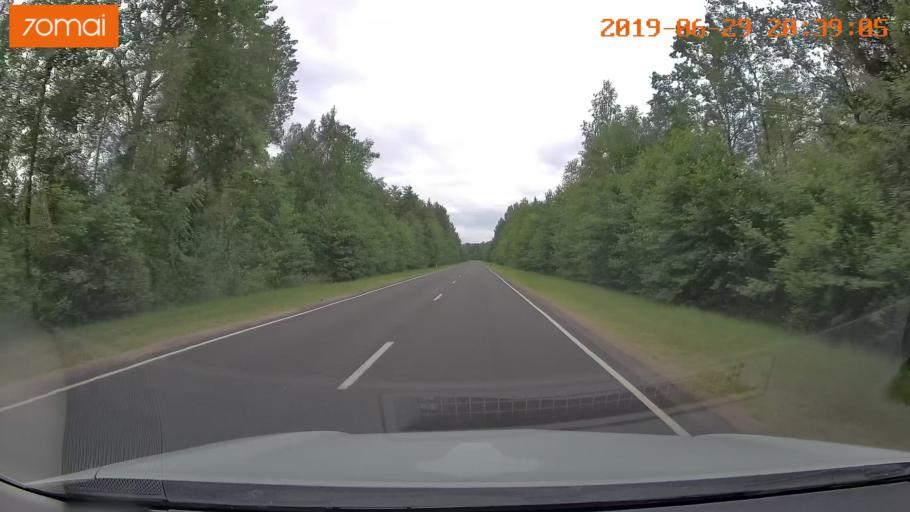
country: BY
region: Brest
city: Hantsavichy
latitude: 52.5579
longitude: 26.3634
